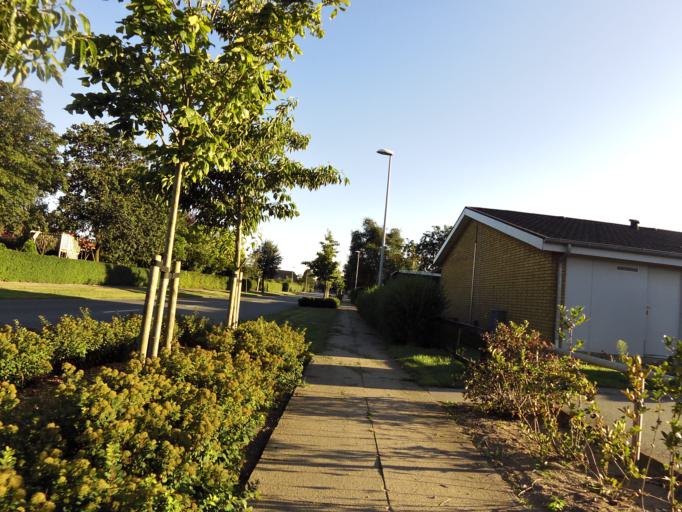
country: DK
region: South Denmark
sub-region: Esbjerg Kommune
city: Ribe
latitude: 55.3415
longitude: 8.7780
